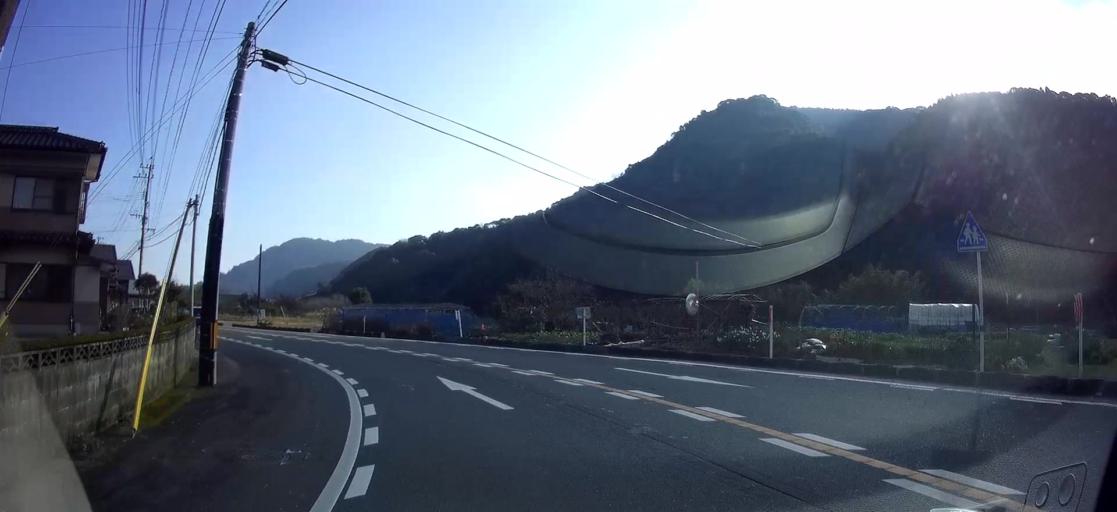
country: JP
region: Kumamoto
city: Hondo
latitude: 32.4311
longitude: 130.3996
